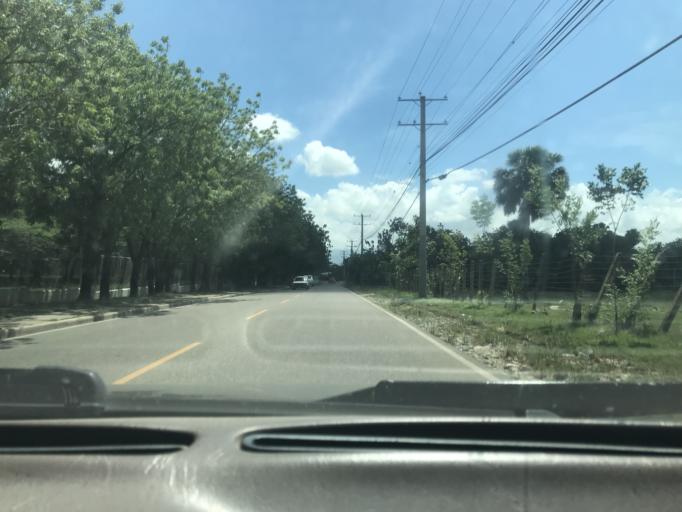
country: DO
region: Santiago
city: Santiago de los Caballeros
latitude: 19.4072
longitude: -70.7204
